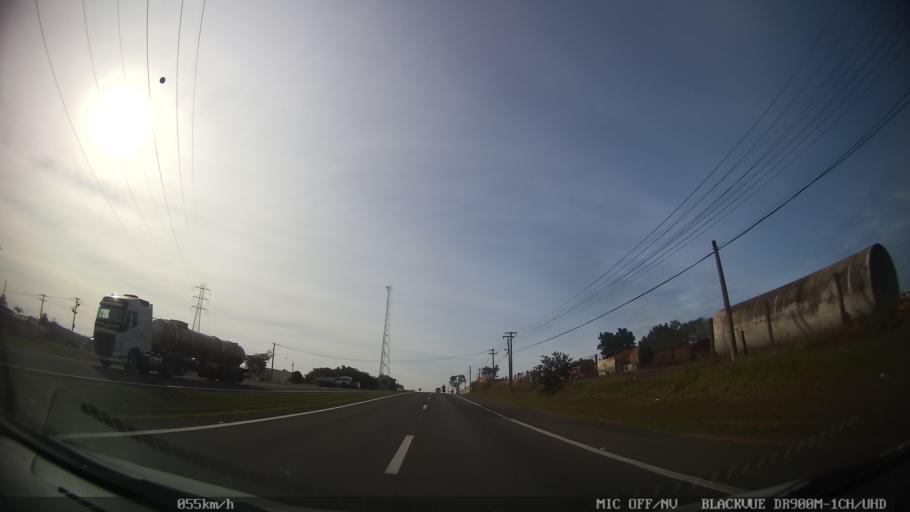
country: BR
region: Sao Paulo
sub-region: Piracicaba
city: Piracicaba
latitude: -22.6789
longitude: -47.7123
